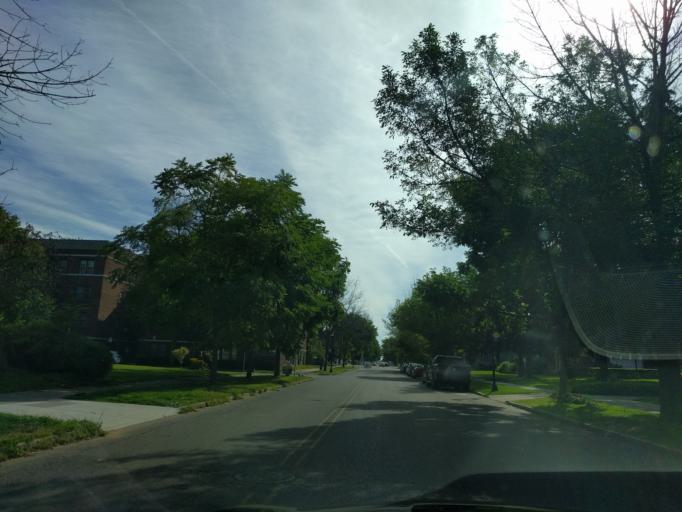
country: US
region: New York
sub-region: Erie County
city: Buffalo
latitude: 42.9048
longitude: -78.8795
